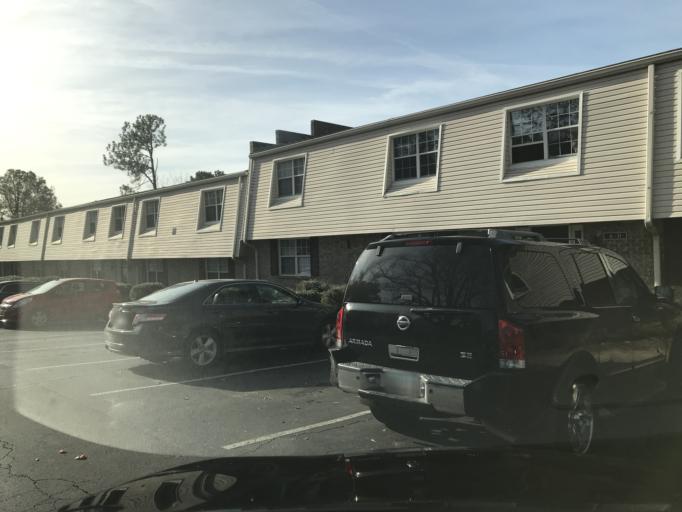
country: US
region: Georgia
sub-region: Clayton County
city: Riverdale
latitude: 33.5796
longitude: -84.3817
